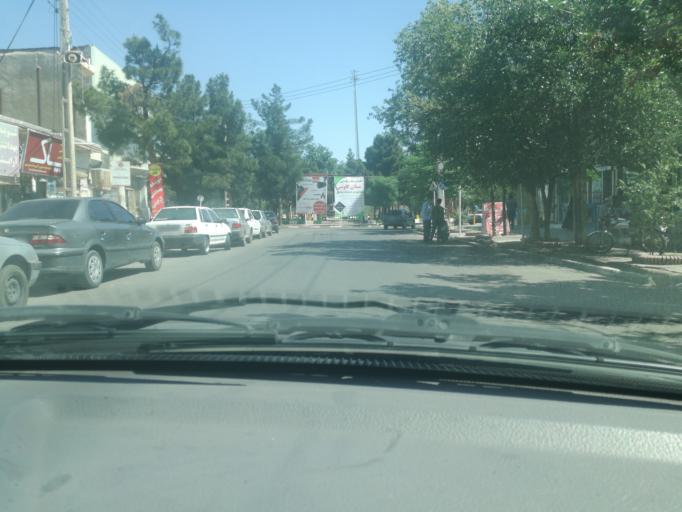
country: IR
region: Razavi Khorasan
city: Sarakhs
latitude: 36.5415
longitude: 61.1638
